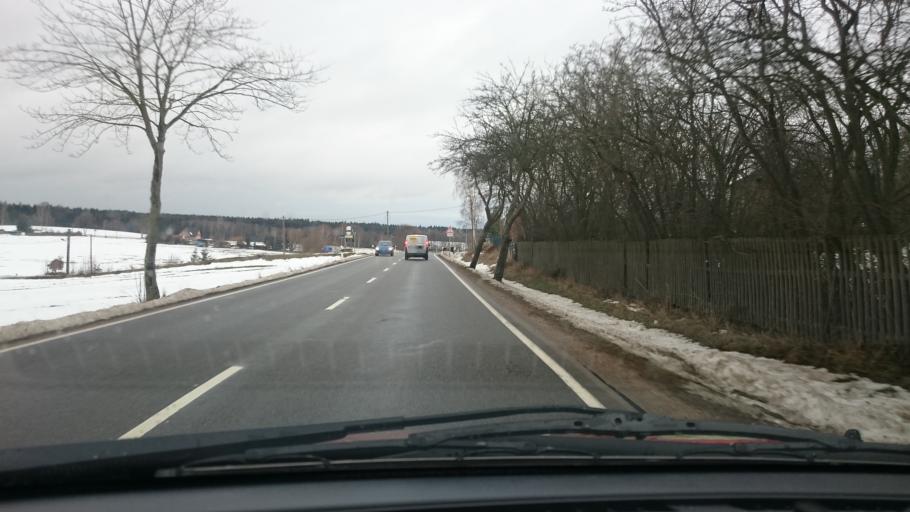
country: DE
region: Saxony
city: Waldkirchen
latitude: 50.6055
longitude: 12.4164
